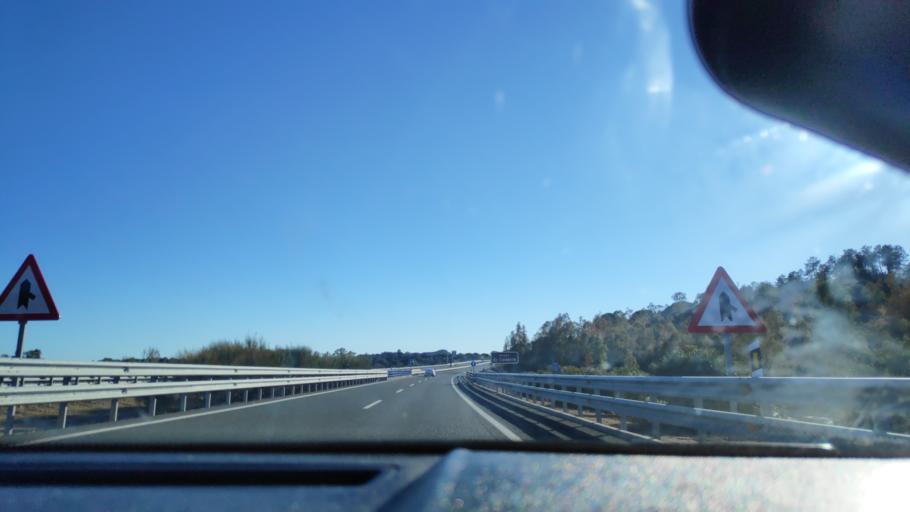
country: ES
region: Extremadura
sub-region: Provincia de Badajoz
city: Monesterio
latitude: 38.0289
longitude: -6.2223
